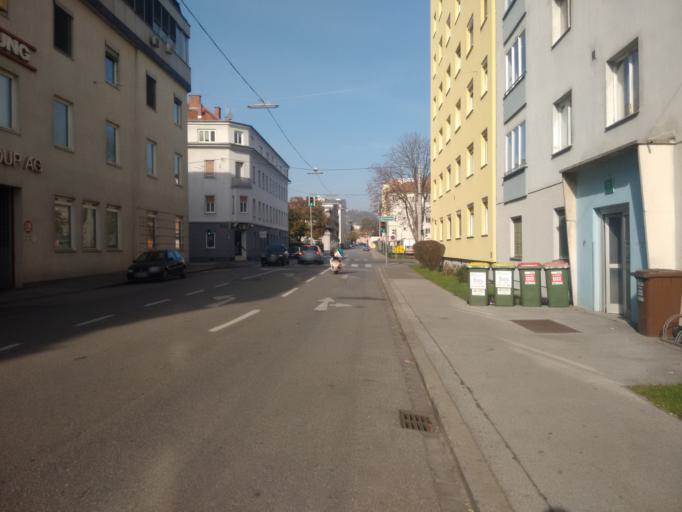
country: AT
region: Styria
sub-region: Graz Stadt
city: Graz
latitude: 47.0598
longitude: 15.4404
